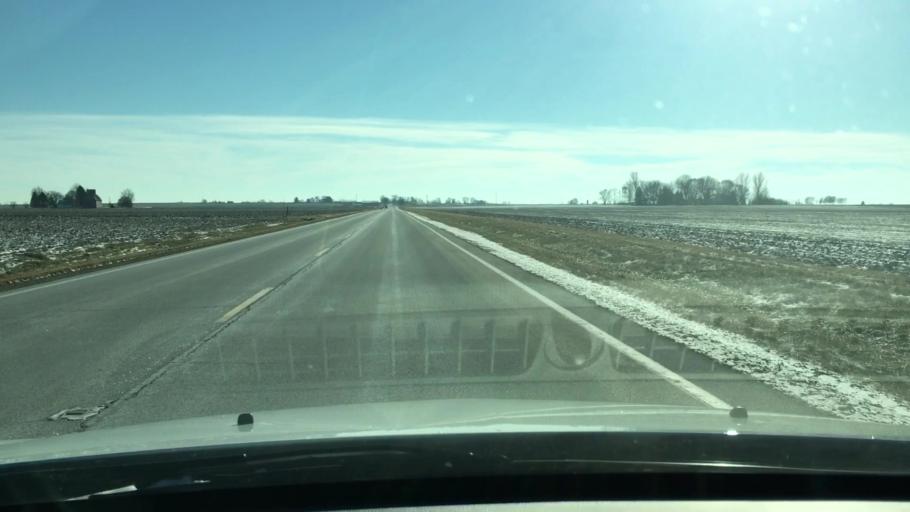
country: US
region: Illinois
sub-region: Ogle County
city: Rochelle
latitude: 41.8533
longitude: -89.0718
